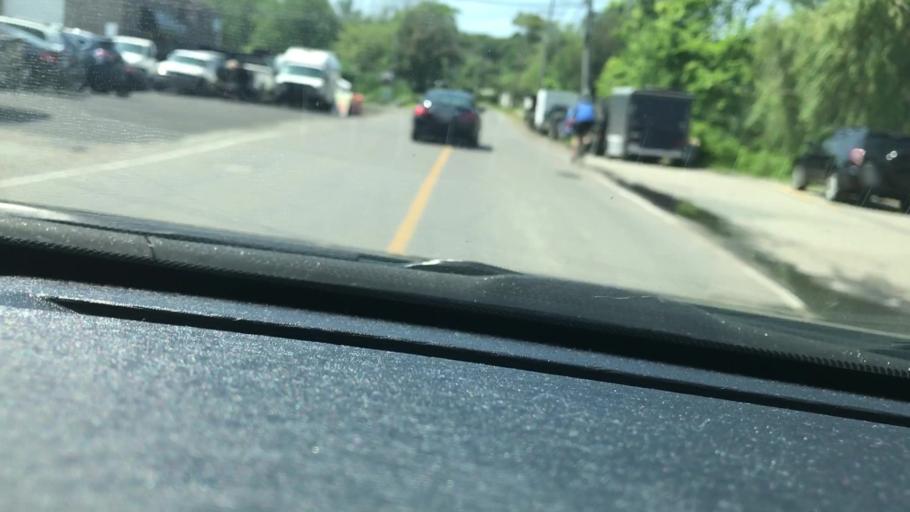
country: US
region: Massachusetts
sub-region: Middlesex County
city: Wakefield
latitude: 42.5083
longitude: -71.0623
